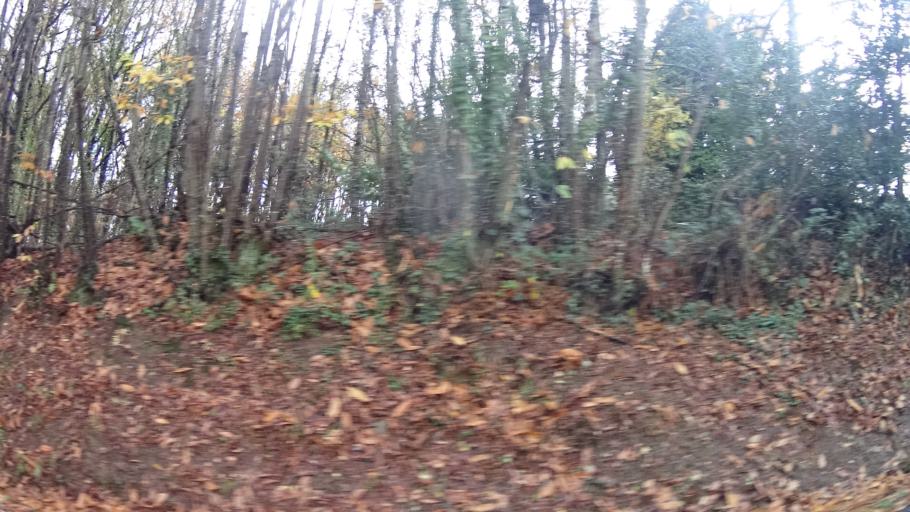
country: FR
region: Pays de la Loire
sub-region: Departement de la Loire-Atlantique
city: Fegreac
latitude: 47.6021
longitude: -2.0647
